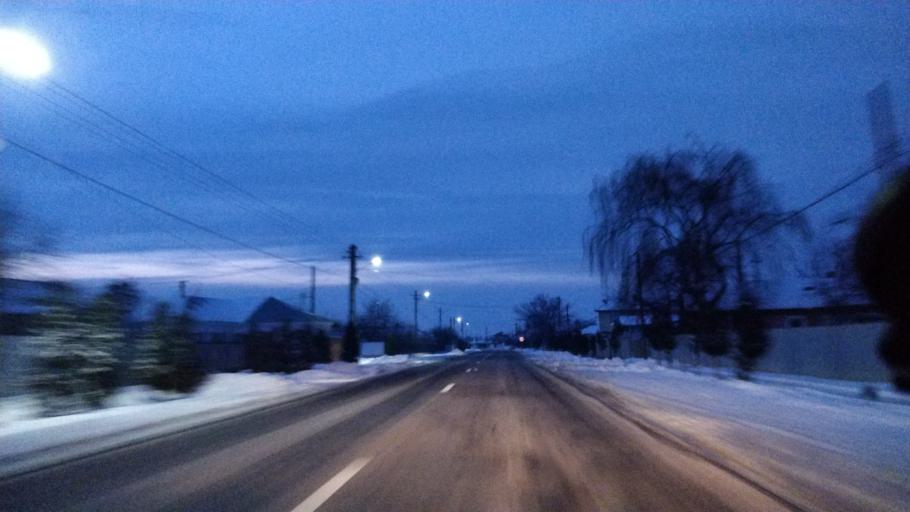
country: RO
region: Vrancea
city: Vulturu de Sus
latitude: 45.6333
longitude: 27.3840
